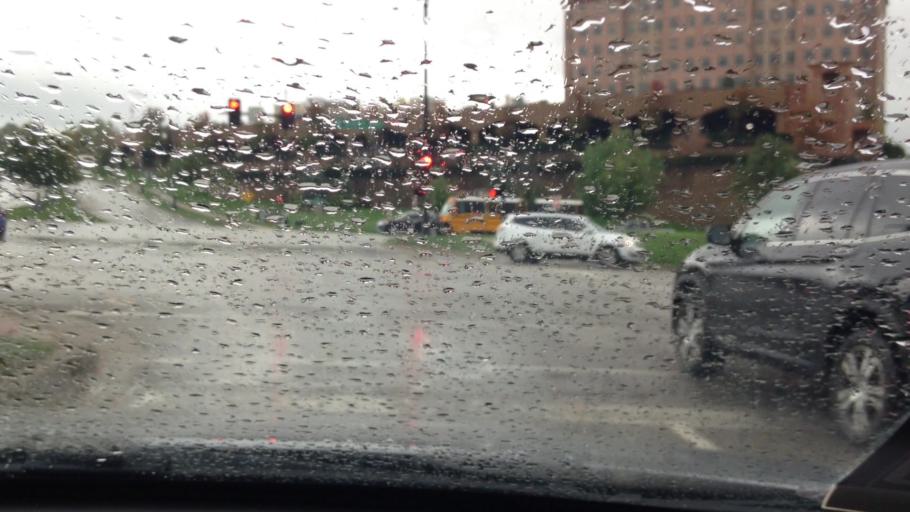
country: US
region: Missouri
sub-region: Platte County
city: Riverside
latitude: 39.1682
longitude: -94.5974
